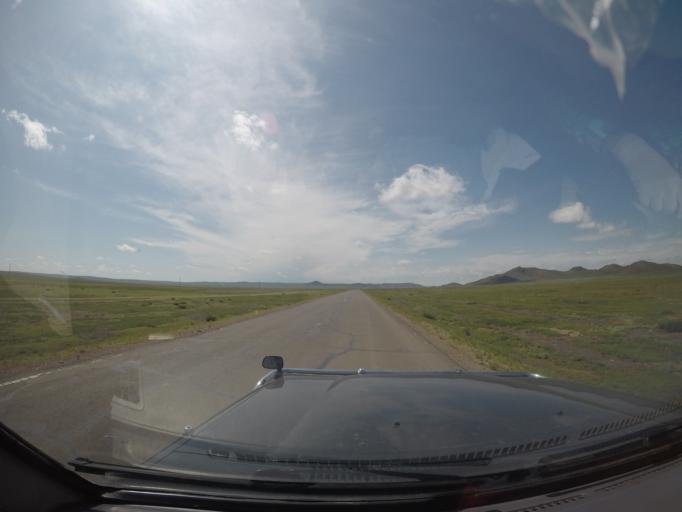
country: MN
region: Hentiy
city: Moron
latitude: 47.3797
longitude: 110.4291
